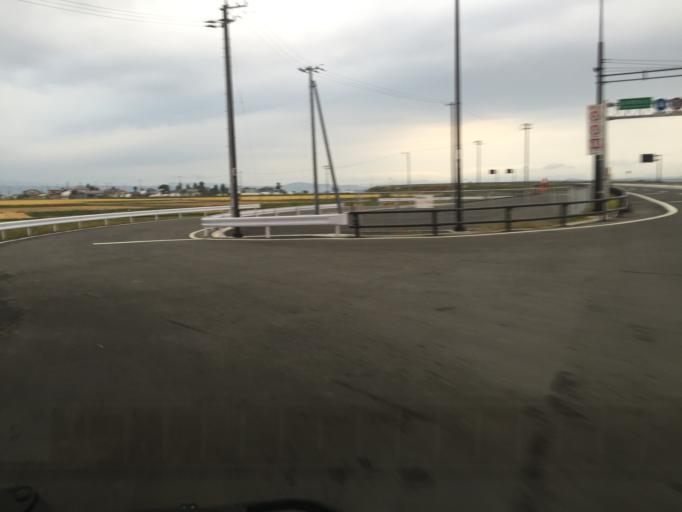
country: JP
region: Fukushima
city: Kitakata
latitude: 37.5350
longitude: 139.9146
